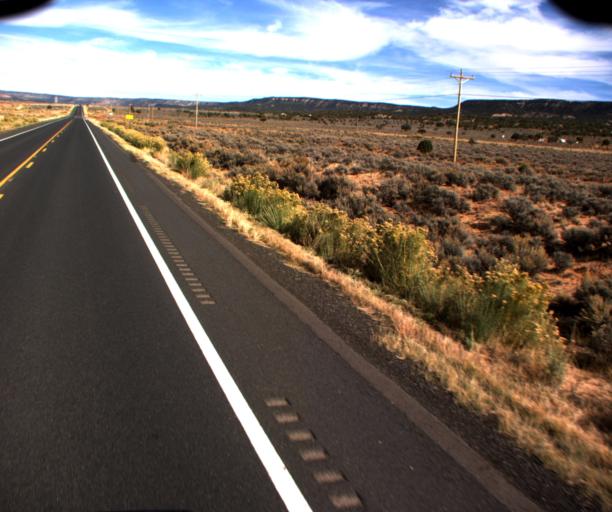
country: US
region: Arizona
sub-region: Navajo County
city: Kayenta
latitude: 36.5201
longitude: -110.5878
